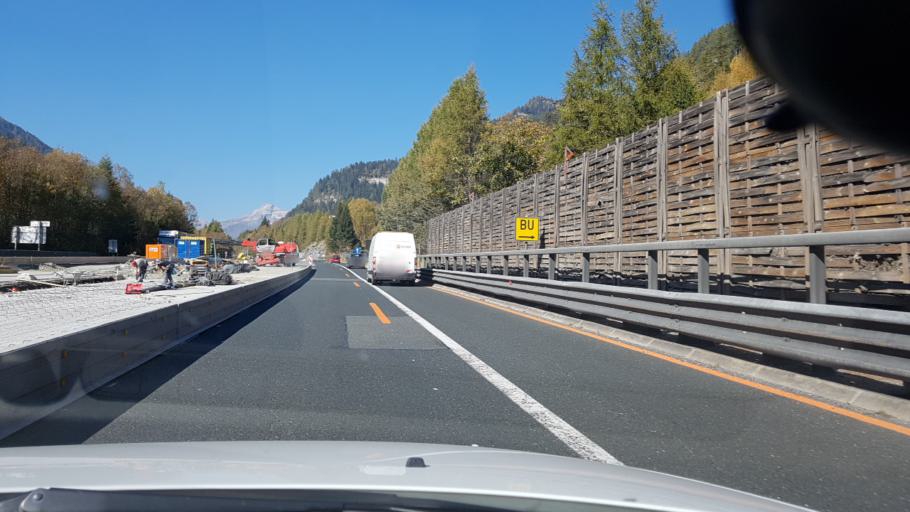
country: AT
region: Salzburg
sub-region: Politischer Bezirk Tamsweg
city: Zederhaus
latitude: 47.1345
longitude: 13.5447
